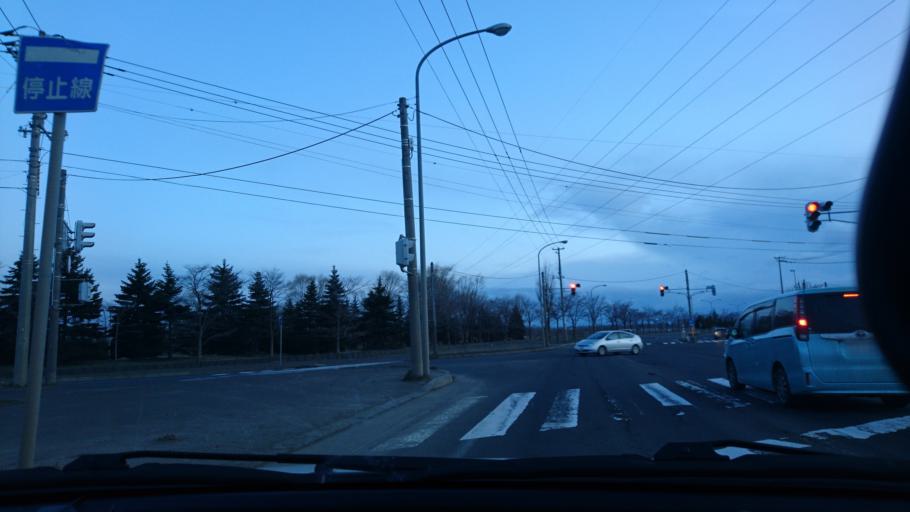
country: JP
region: Hokkaido
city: Sapporo
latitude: 43.1286
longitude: 141.4188
